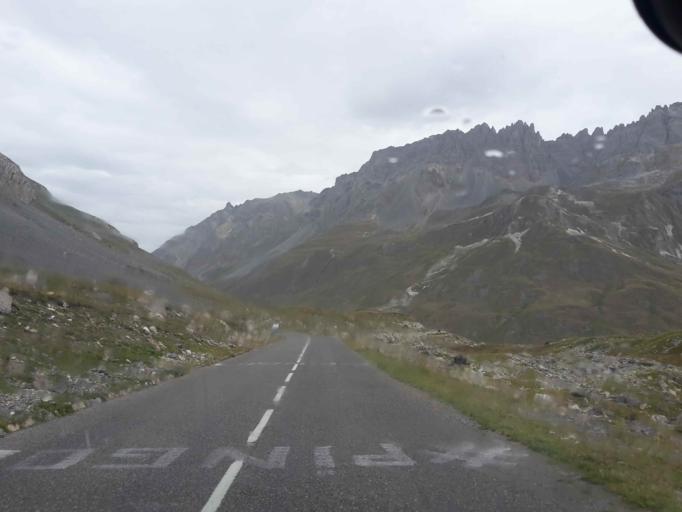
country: FR
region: Rhone-Alpes
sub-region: Departement de la Savoie
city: Valloire
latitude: 45.0816
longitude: 6.4263
